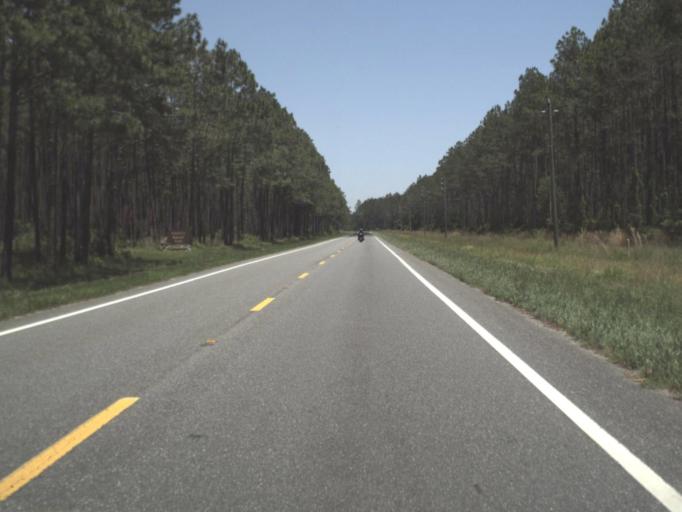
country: US
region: Florida
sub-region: Columbia County
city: Watertown
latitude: 30.1884
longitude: -82.5457
